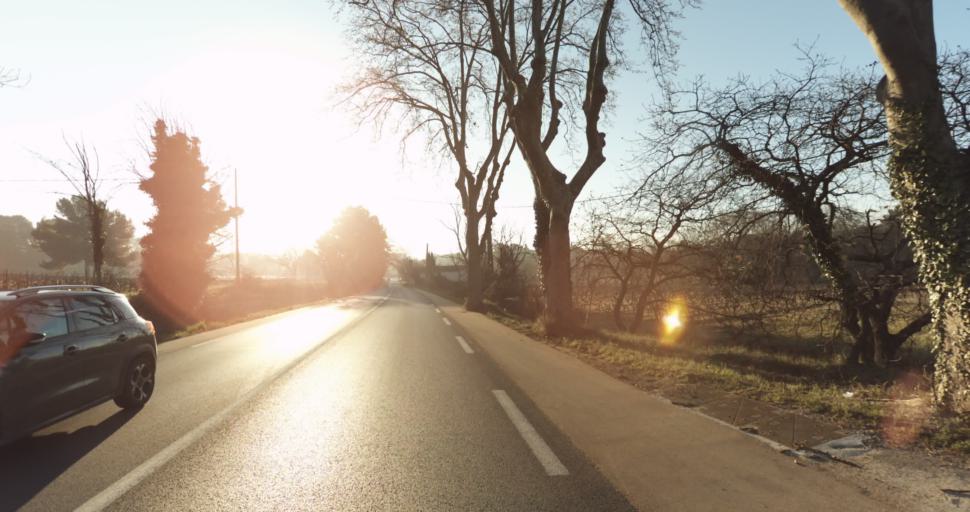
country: FR
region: Provence-Alpes-Cote d'Azur
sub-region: Departement des Bouches-du-Rhone
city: Eguilles
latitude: 43.5362
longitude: 5.3885
